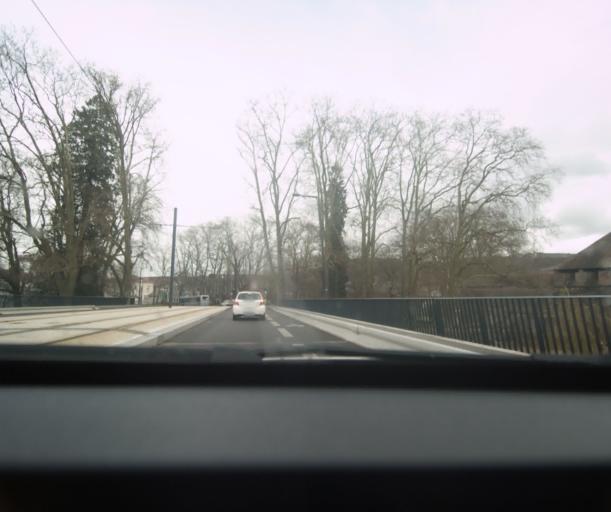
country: FR
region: Franche-Comte
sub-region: Departement du Doubs
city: Besancon
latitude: 47.2312
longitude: 6.0178
